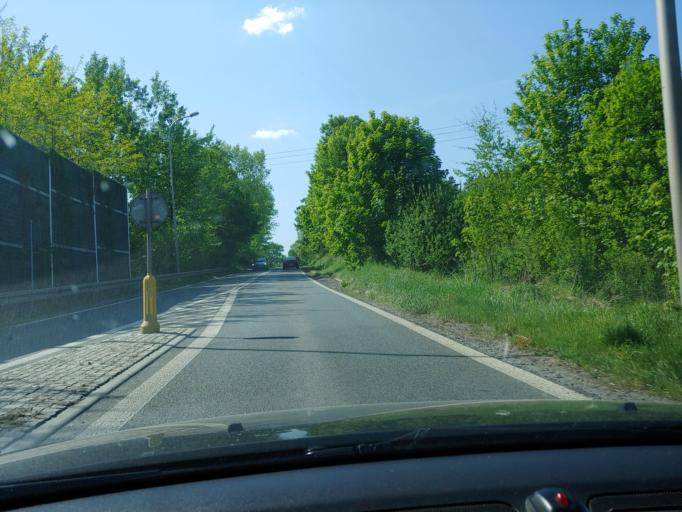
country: PL
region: Lesser Poland Voivodeship
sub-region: Powiat chrzanowski
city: Libiaz
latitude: 50.1576
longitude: 19.3273
